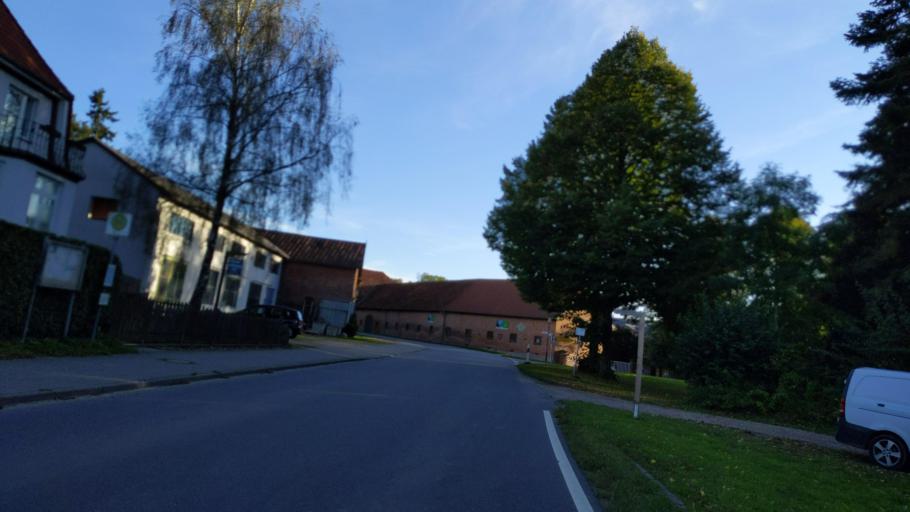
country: DE
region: Schleswig-Holstein
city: Glasau
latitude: 54.0496
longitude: 10.5597
